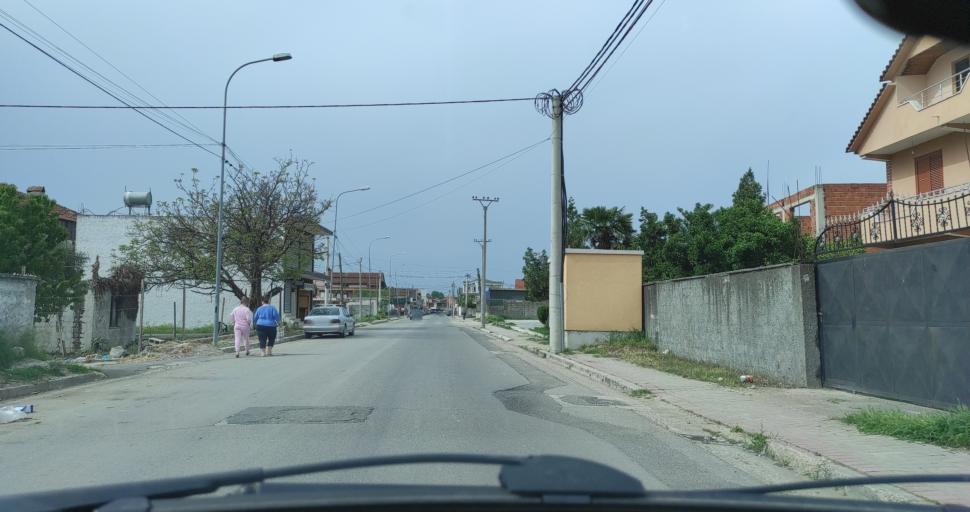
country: AL
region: Durres
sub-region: Rrethi i Krujes
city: Fushe-Kruje
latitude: 41.4752
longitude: 19.7183
